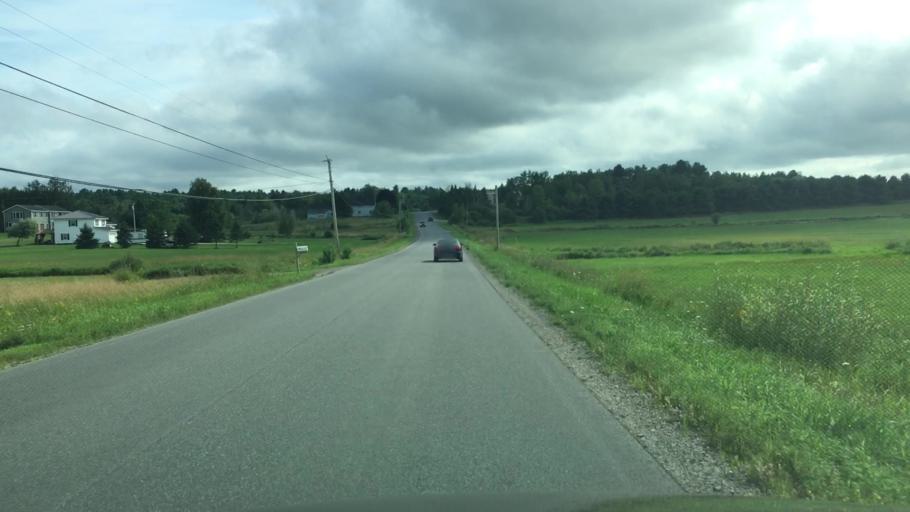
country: US
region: Maine
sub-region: Waldo County
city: Winterport
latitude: 44.6743
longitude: -68.8682
